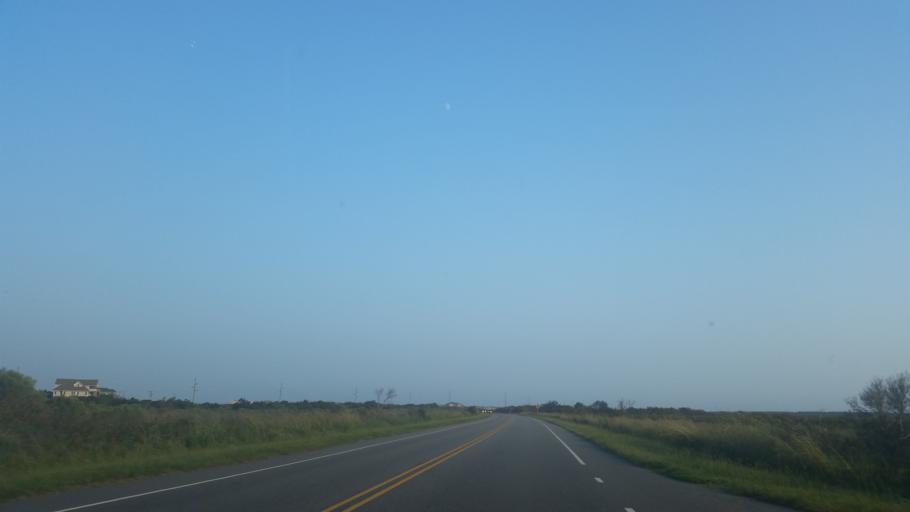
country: US
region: North Carolina
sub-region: Dare County
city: Wanchese
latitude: 35.8479
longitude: -75.5699
